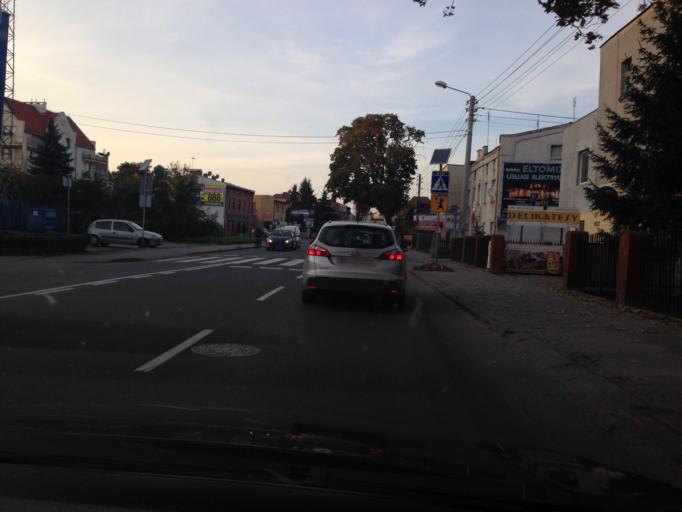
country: PL
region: Kujawsko-Pomorskie
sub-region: Powiat inowroclawski
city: Inowroclaw
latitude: 52.7902
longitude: 18.2652
